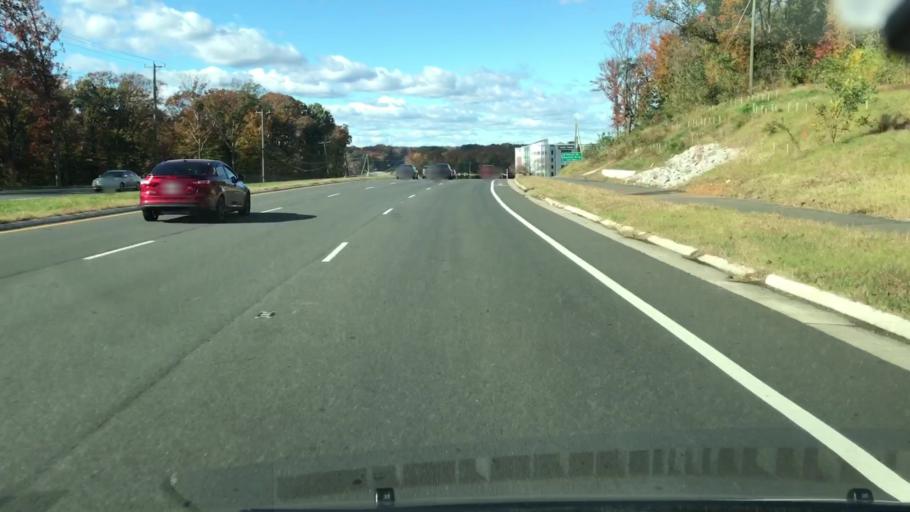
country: US
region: Virginia
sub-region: Fairfax County
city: Fort Belvoir
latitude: 38.7090
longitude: -77.1549
